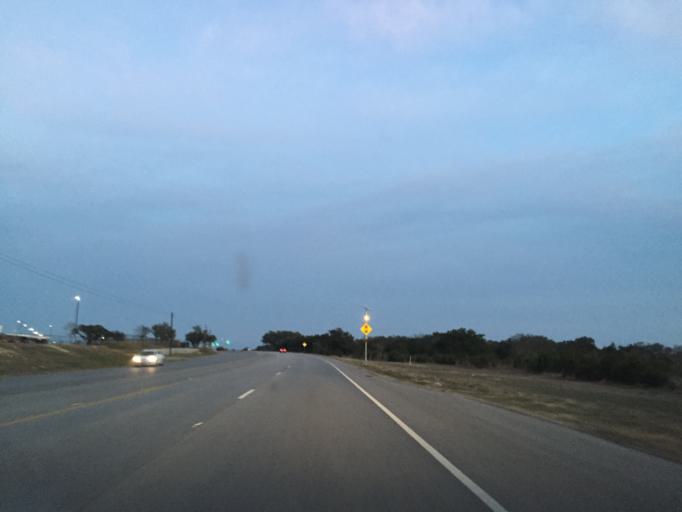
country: US
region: Texas
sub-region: Burnet County
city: Bertram
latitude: 30.6825
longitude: -97.9590
